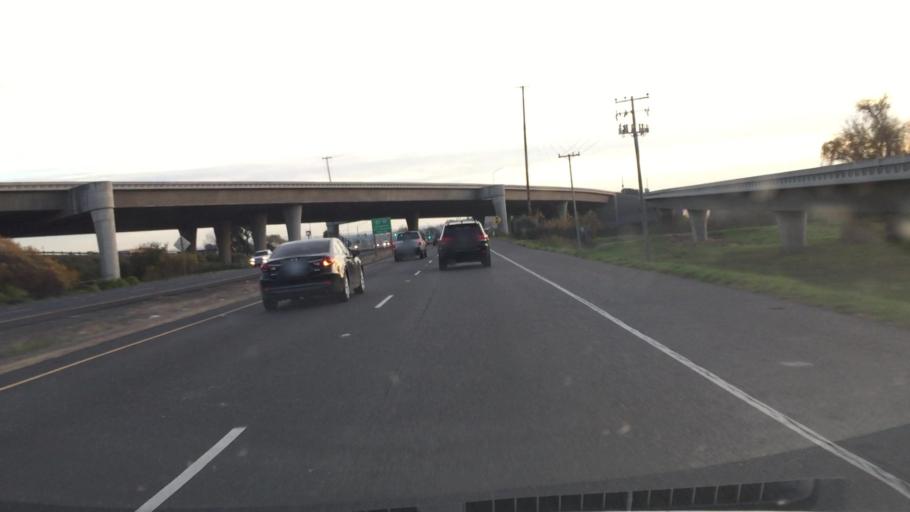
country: US
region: California
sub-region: Napa County
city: American Canyon
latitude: 38.1418
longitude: -122.2559
